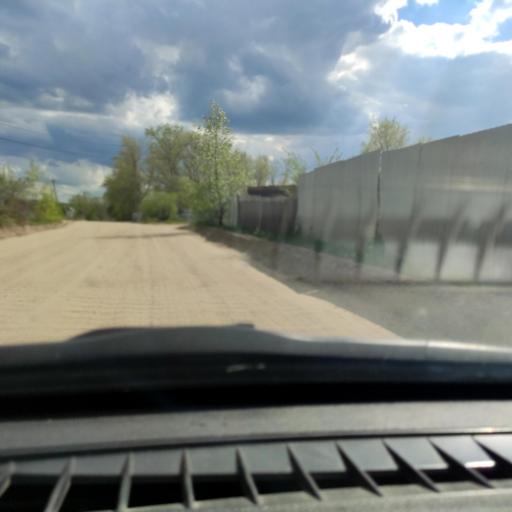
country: RU
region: Samara
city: Zhigulevsk
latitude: 53.4534
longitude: 49.5349
